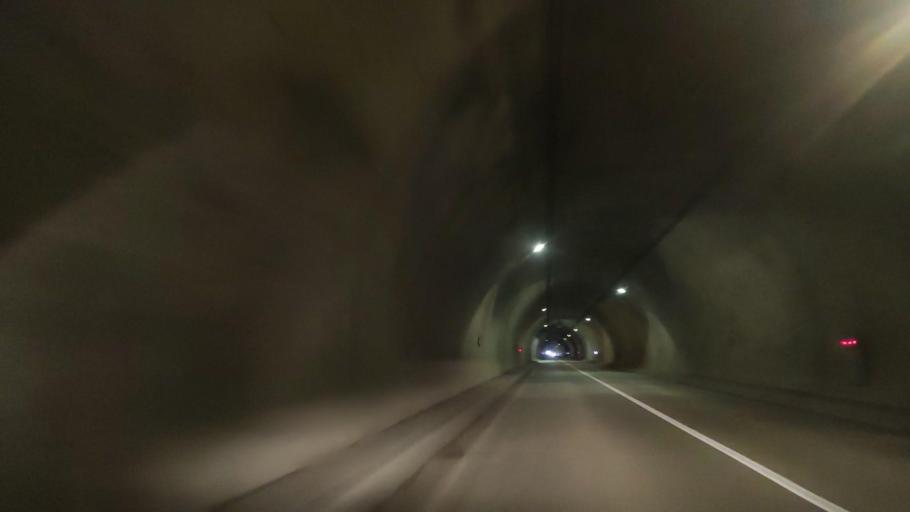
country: JP
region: Hokkaido
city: Iwamizawa
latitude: 43.0299
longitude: 142.0890
